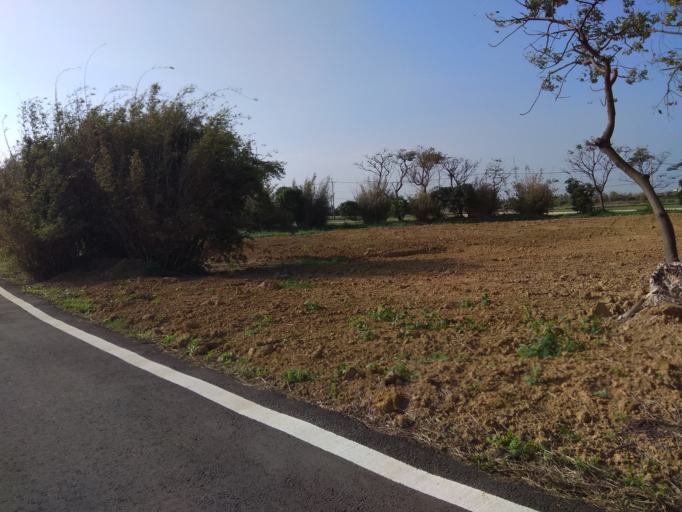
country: TW
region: Taiwan
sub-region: Hsinchu
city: Zhubei
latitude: 25.0057
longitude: 121.0462
